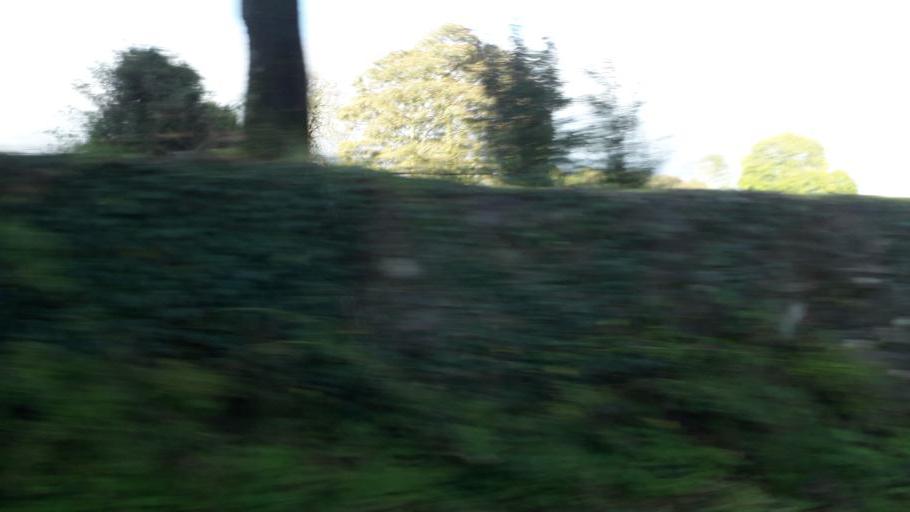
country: IE
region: Connaught
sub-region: Roscommon
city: Castlerea
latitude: 53.8726
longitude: -8.4180
